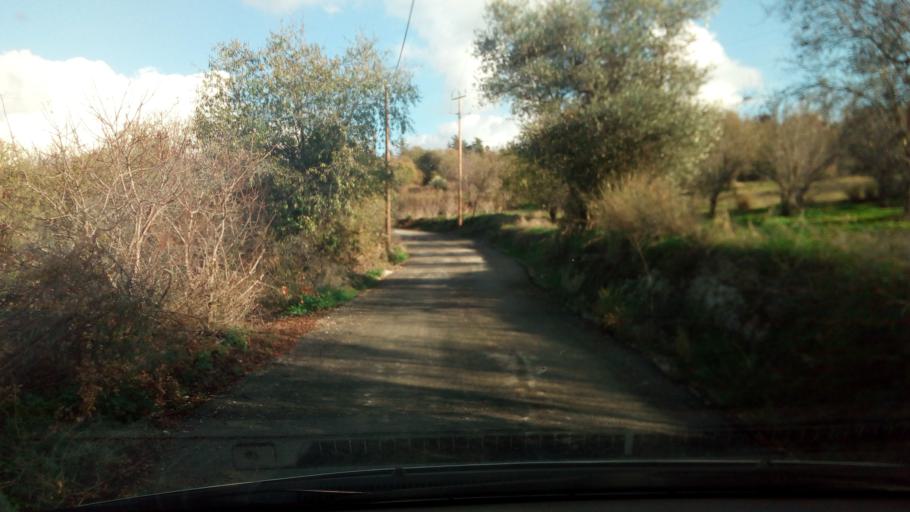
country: CY
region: Pafos
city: Polis
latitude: 34.9402
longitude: 32.4998
